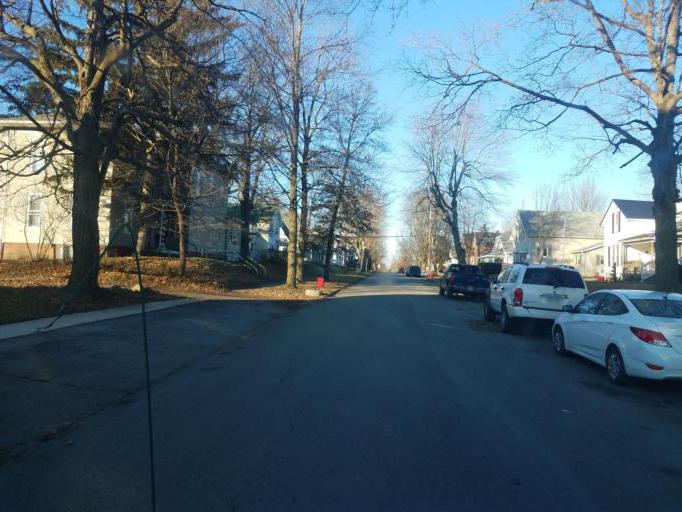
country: US
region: Ohio
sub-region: Hardin County
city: Kenton
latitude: 40.6507
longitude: -83.6056
